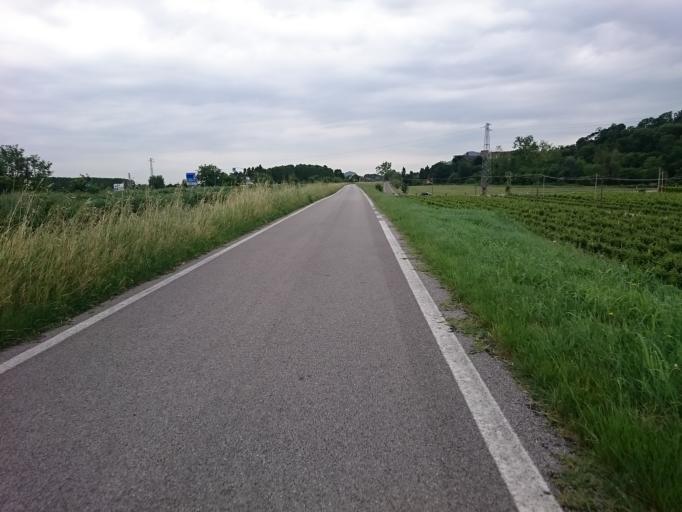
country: IT
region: Veneto
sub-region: Provincia di Padova
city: Battaglia Terme
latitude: 45.3015
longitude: 11.7933
